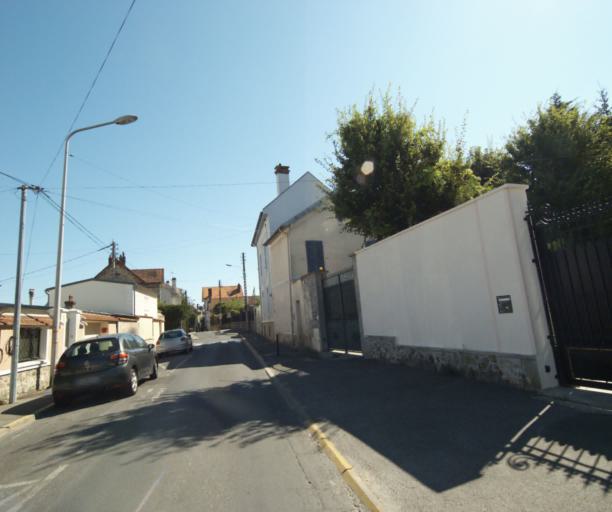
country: FR
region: Ile-de-France
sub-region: Departement de Seine-et-Marne
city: Lagny-sur-Marne
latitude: 48.8774
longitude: 2.7086
